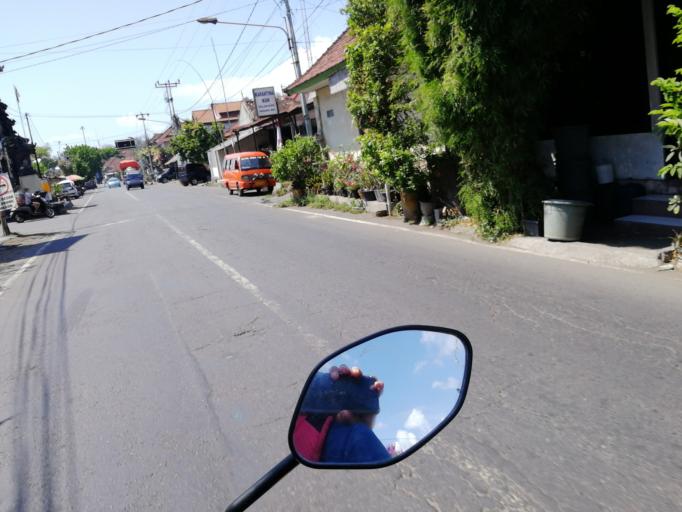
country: ID
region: Bali
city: Padangbai
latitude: -8.5310
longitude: 115.5061
